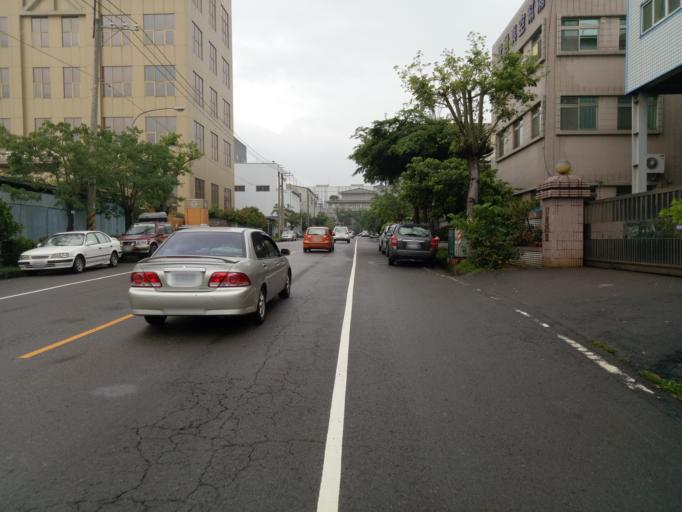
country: TW
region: Taiwan
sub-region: Taichung City
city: Taichung
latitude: 24.1054
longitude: 120.7168
